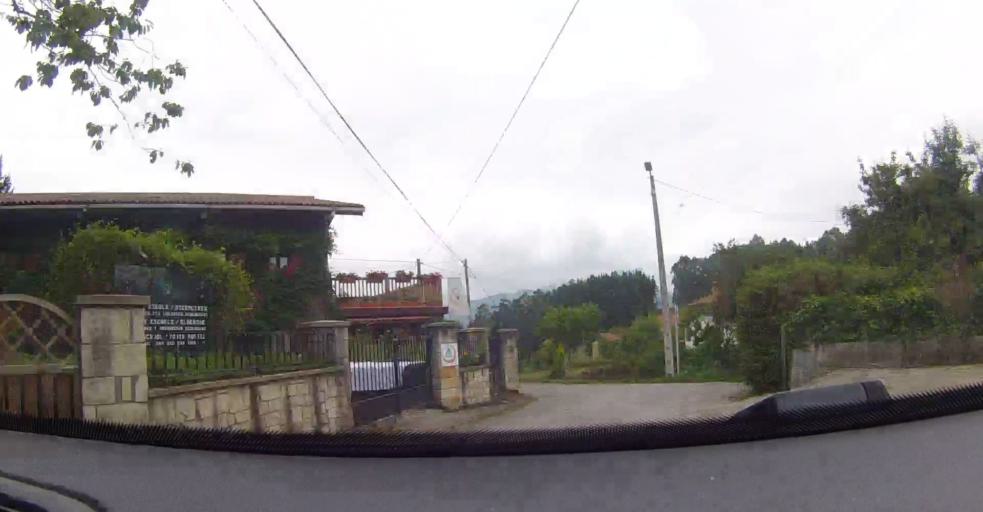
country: ES
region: Basque Country
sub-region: Bizkaia
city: Sopuerta
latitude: 43.2589
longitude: -3.1365
